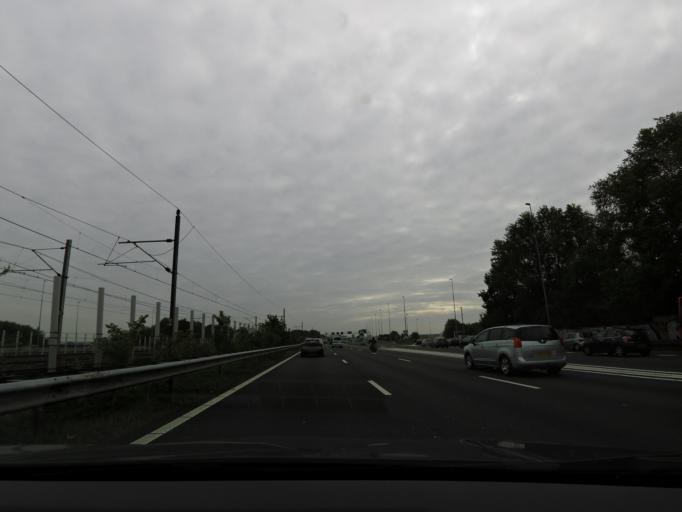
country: NL
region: North Holland
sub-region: Gemeente Amstelveen
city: Amstelveen
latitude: 52.3316
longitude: 4.8003
